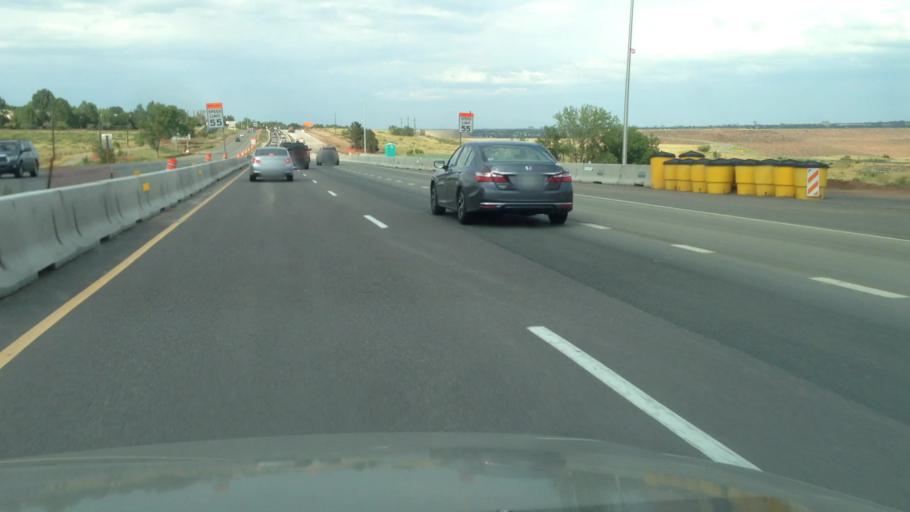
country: US
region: Colorado
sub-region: Jefferson County
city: Columbine
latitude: 39.5579
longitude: -105.0784
